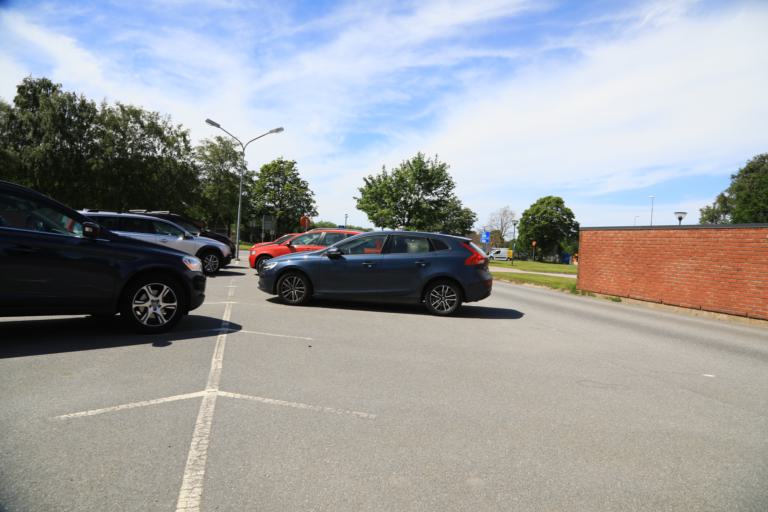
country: SE
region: Halland
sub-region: Varbergs Kommun
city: Varberg
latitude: 57.1005
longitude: 12.2757
